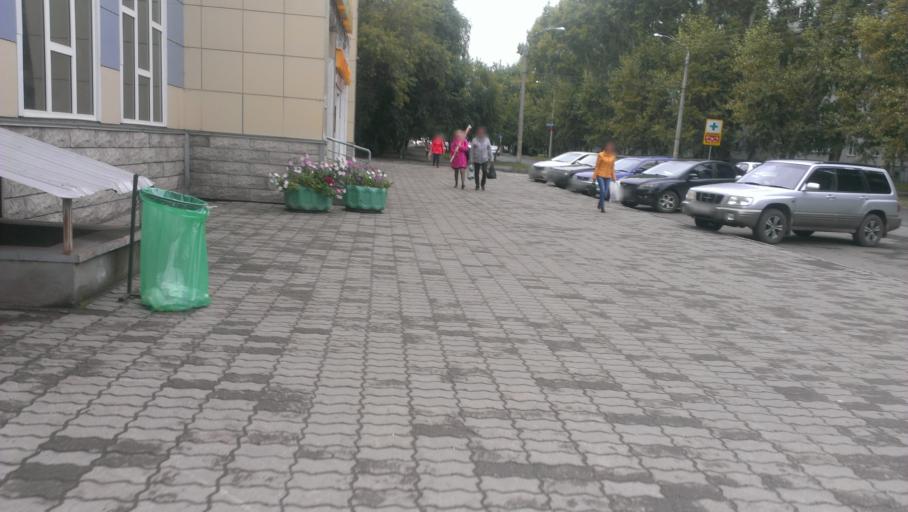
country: RU
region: Altai Krai
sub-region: Gorod Barnaulskiy
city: Barnaul
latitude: 53.3710
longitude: 83.6813
